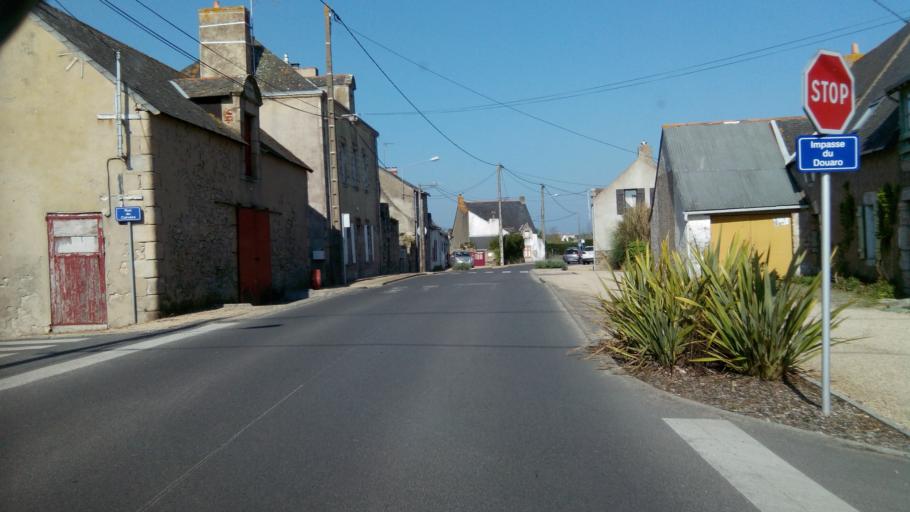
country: FR
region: Pays de la Loire
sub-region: Departement de la Loire-Atlantique
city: Batz-sur-Mer
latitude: 47.2780
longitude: -2.4535
